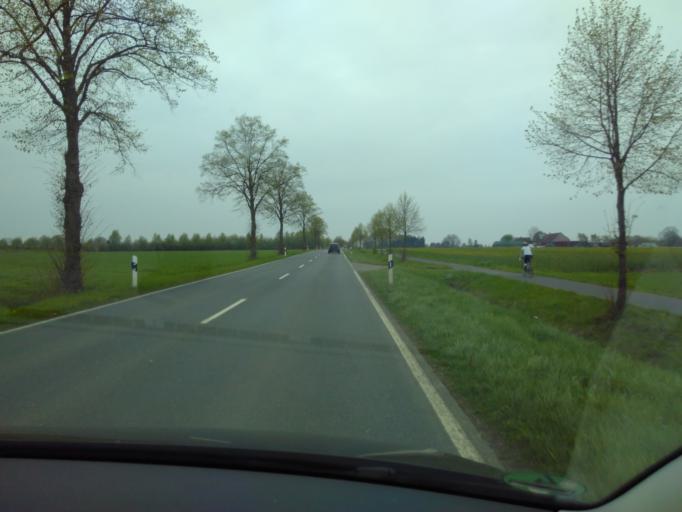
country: DE
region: North Rhine-Westphalia
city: Oelde
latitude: 51.7780
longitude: 8.1483
